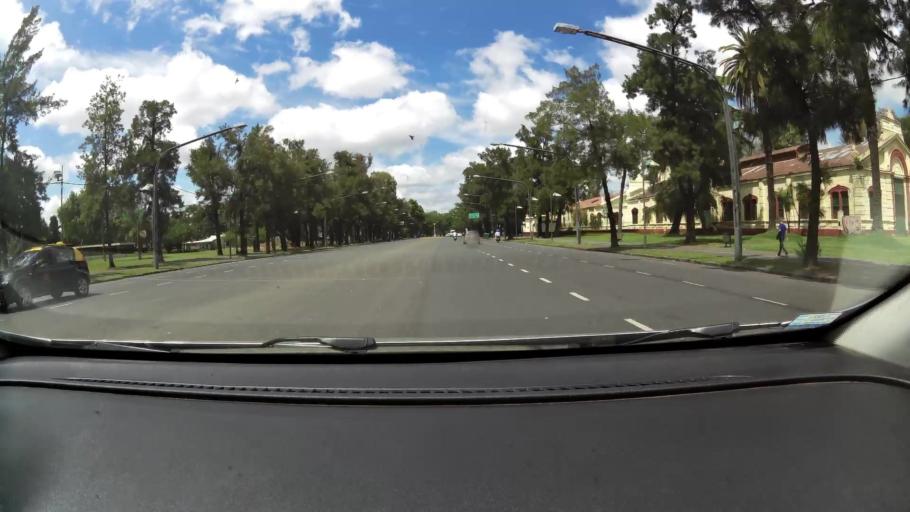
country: AR
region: Santa Fe
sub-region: Departamento de Rosario
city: Rosario
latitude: -32.9631
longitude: -60.6582
